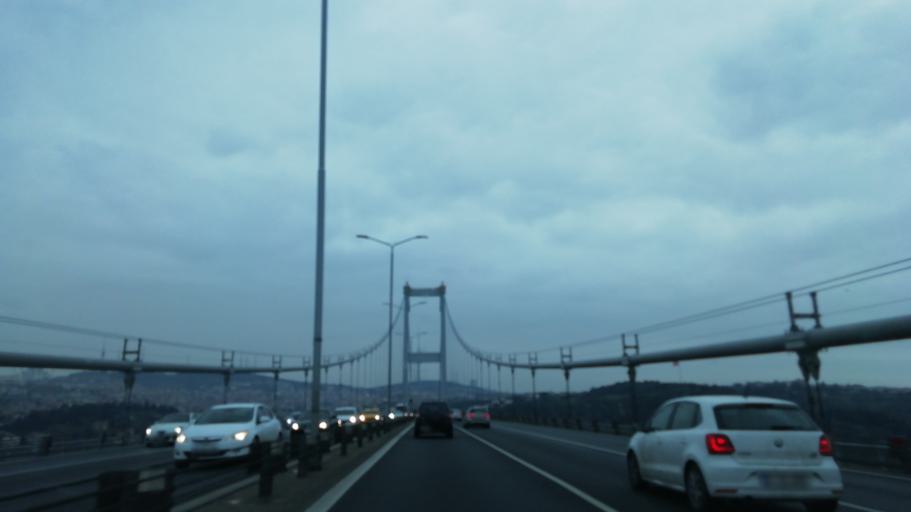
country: TR
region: Istanbul
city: UEskuedar
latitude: 41.0454
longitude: 29.0344
